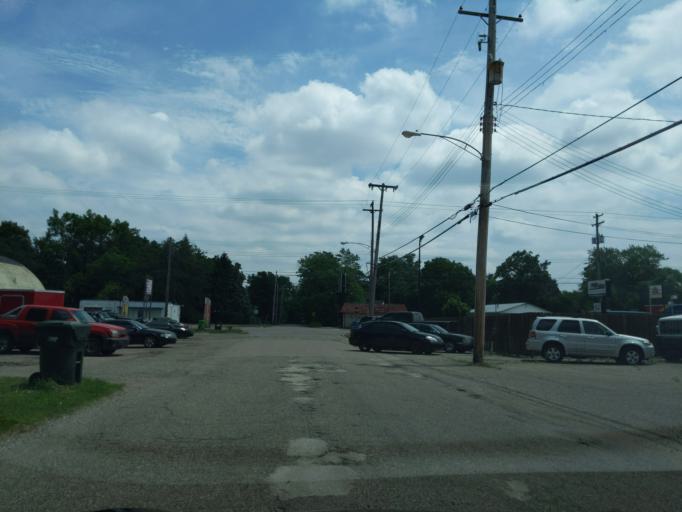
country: US
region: Michigan
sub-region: Ingham County
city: Lansing
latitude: 42.7679
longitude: -84.5437
